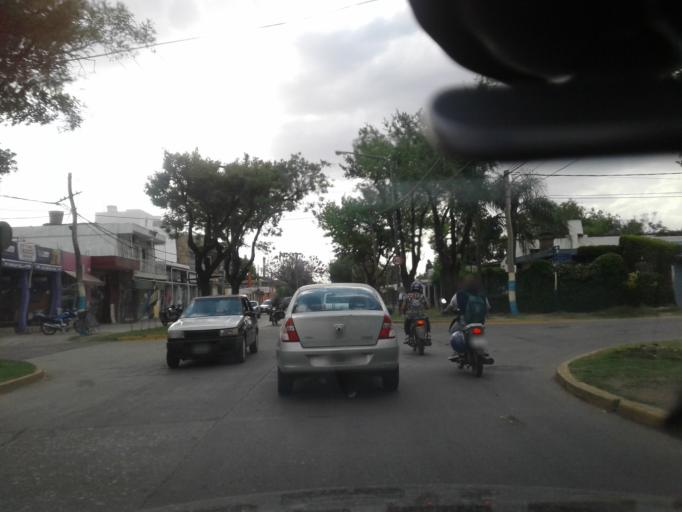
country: AR
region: Santa Fe
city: Granadero Baigorria
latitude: -32.8938
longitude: -60.7125
